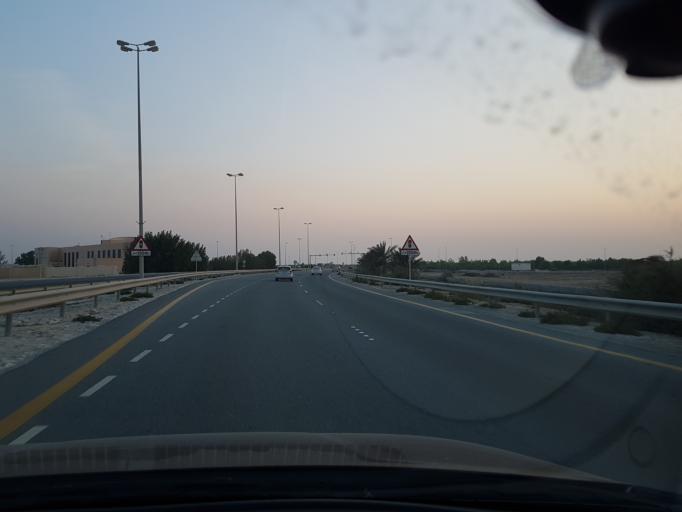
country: BH
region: Central Governorate
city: Dar Kulayb
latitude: 26.0180
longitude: 50.4884
